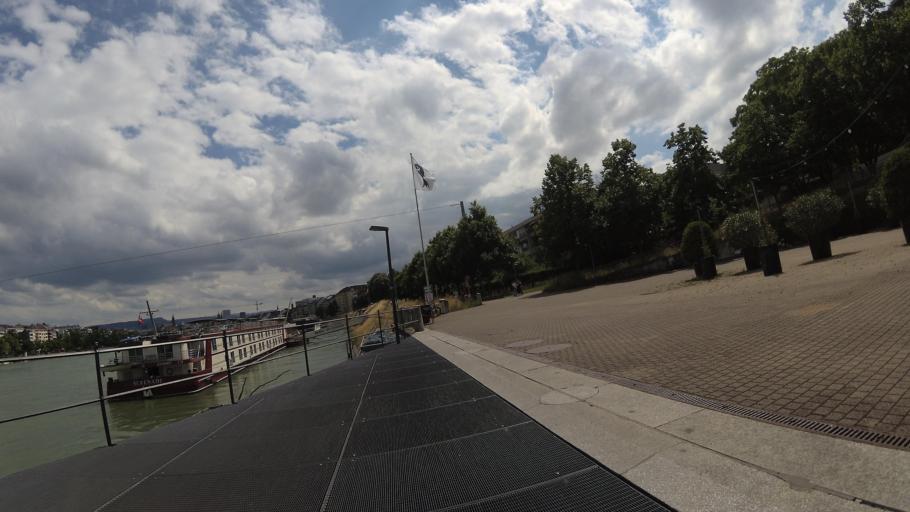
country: CH
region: Basel-City
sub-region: Basel-Stadt
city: Basel
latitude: 47.5696
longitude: 7.5834
